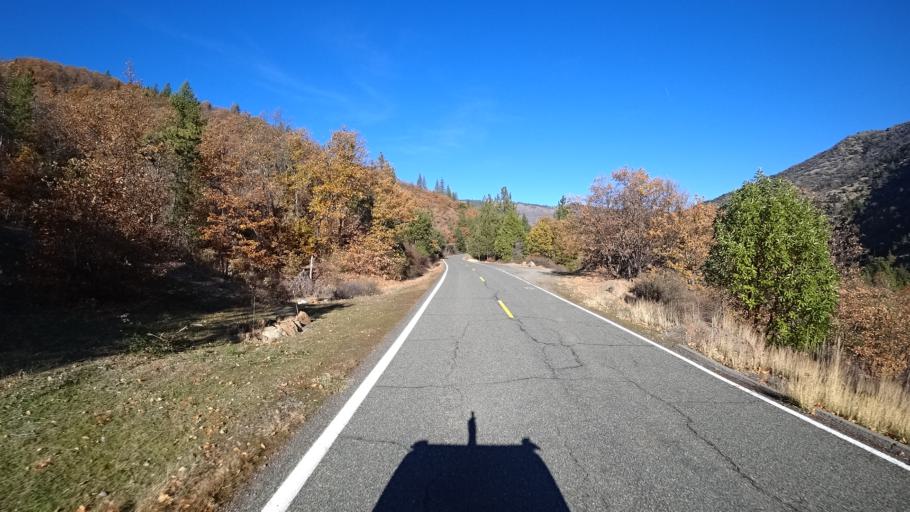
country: US
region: California
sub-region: Siskiyou County
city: Yreka
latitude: 41.8995
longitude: -122.8282
